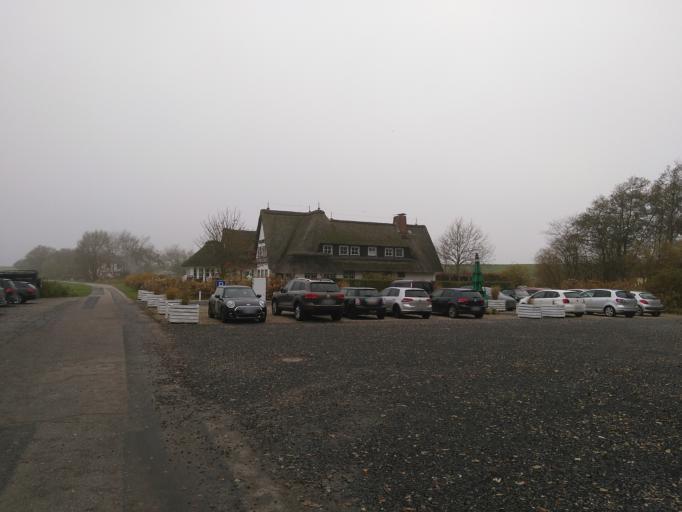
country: DE
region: Schleswig-Holstein
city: Simonsberg
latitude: 54.4538
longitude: 8.9680
